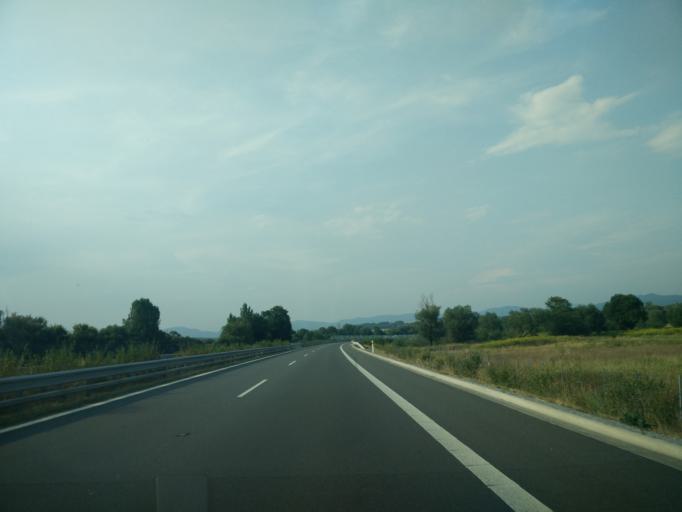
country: SK
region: Banskobystricky
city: Ziar nad Hronom
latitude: 48.5604
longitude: 18.8203
